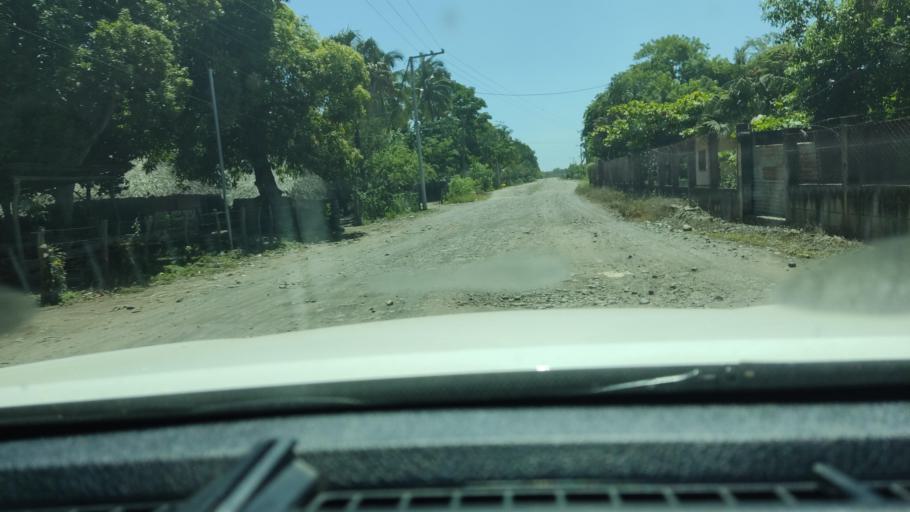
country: SV
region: Ahuachapan
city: San Francisco Menendez
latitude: 13.7513
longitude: -90.1224
